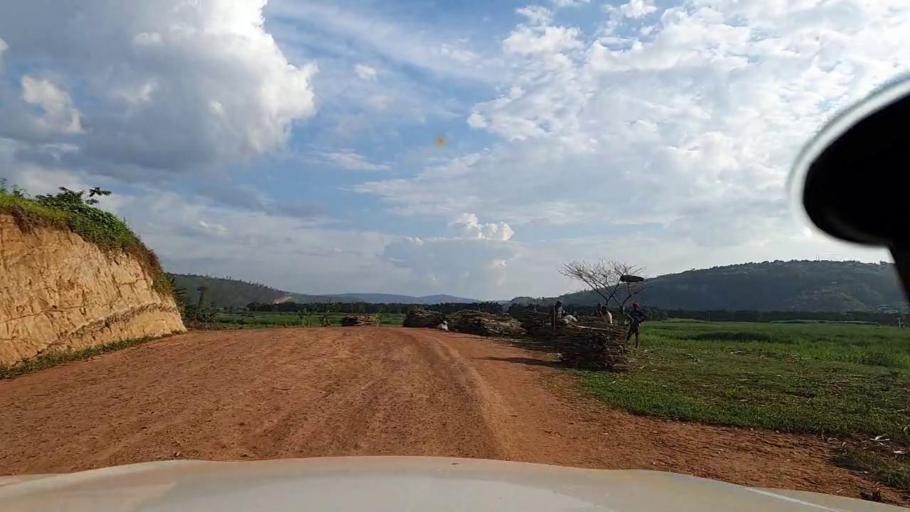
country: RW
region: Kigali
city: Kigali
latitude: -1.9316
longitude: 29.9957
